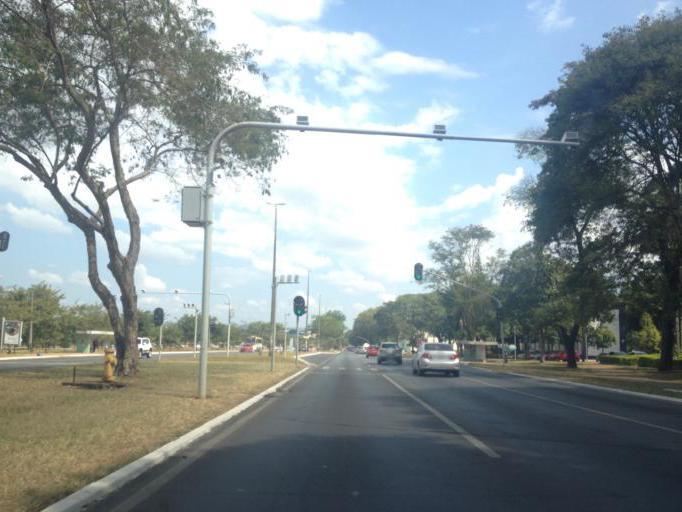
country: BR
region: Federal District
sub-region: Brasilia
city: Brasilia
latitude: -15.8308
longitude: -47.9089
